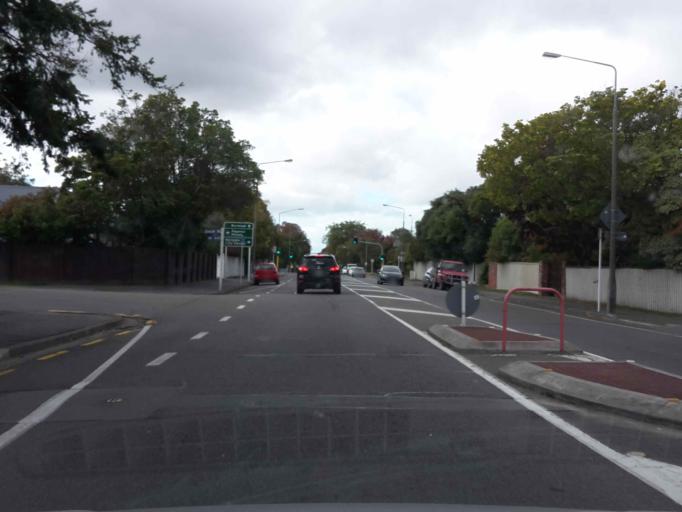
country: NZ
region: Canterbury
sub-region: Christchurch City
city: Christchurch
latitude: -43.5100
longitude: 172.6175
